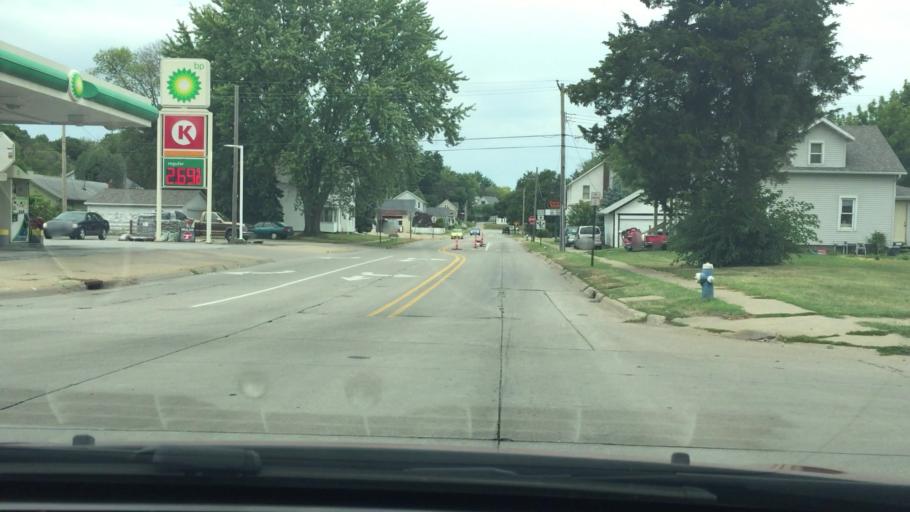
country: US
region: Iowa
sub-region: Muscatine County
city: Muscatine
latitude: 41.4314
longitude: -91.0409
